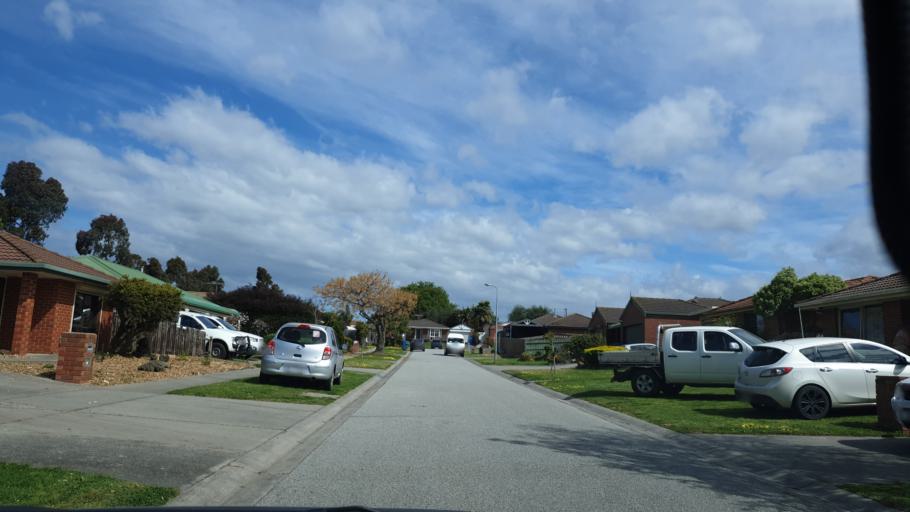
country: AU
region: Victoria
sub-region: Casey
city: Cranbourne North
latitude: -38.0800
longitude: 145.2956
